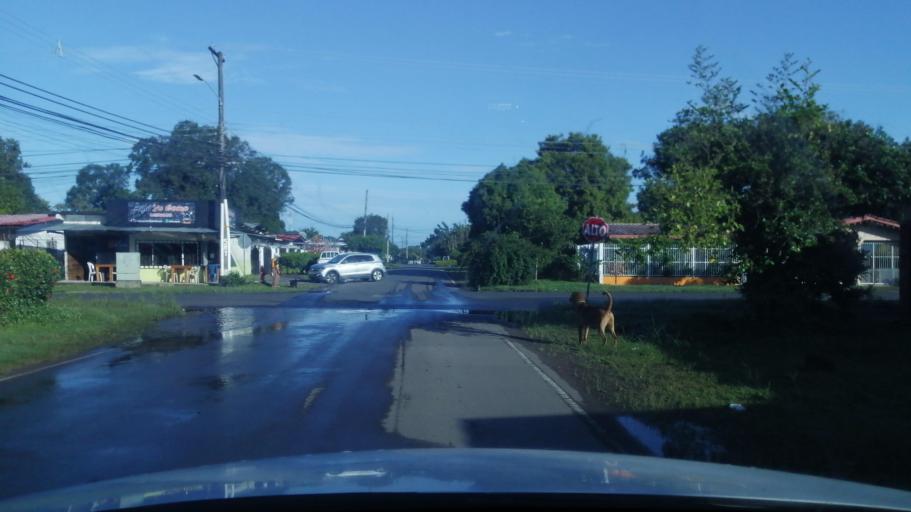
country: PA
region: Chiriqui
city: David
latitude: 8.4239
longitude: -82.4357
